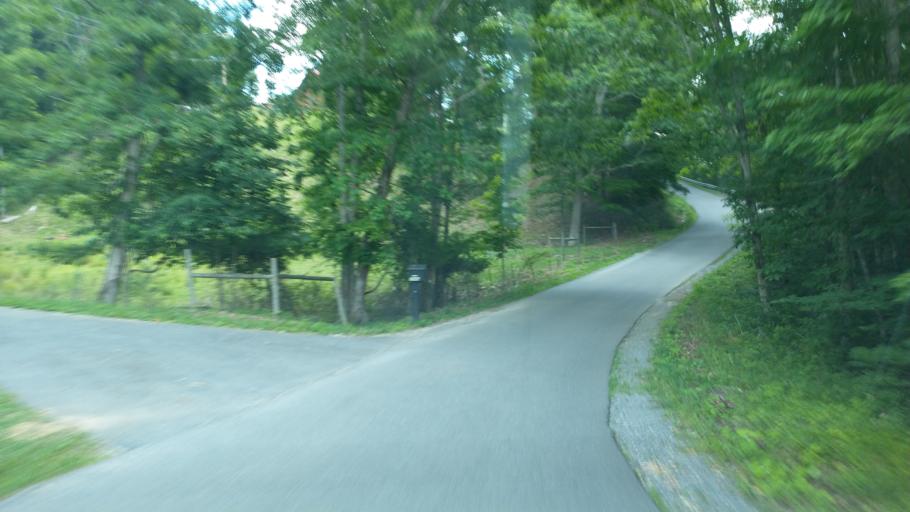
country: US
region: West Virginia
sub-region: Mercer County
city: Athens
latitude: 37.4612
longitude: -81.0550
